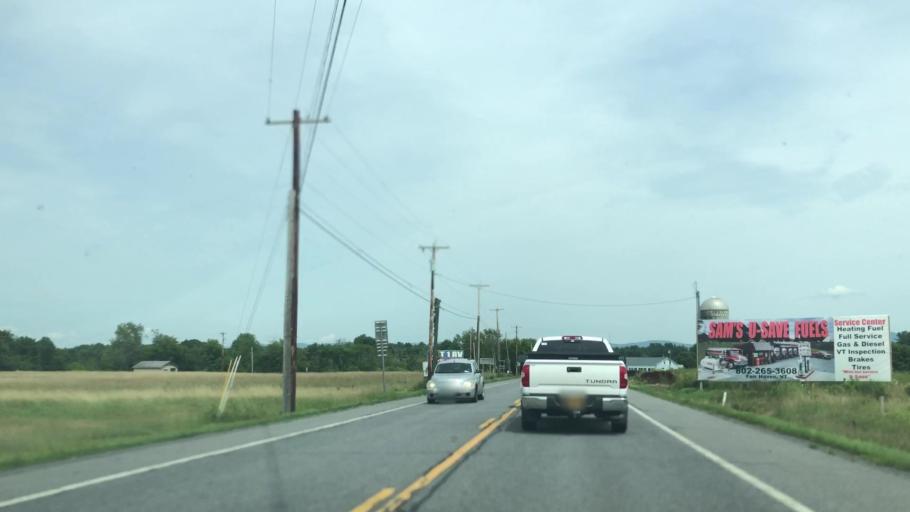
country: US
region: Vermont
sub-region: Rutland County
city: Fair Haven
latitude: 43.5852
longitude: -73.3003
